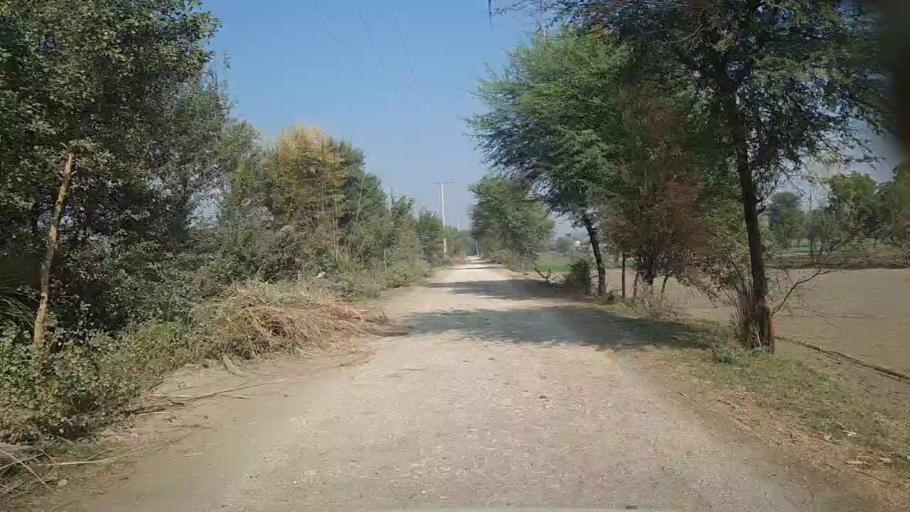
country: PK
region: Sindh
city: Karaundi
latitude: 26.9586
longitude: 68.4192
